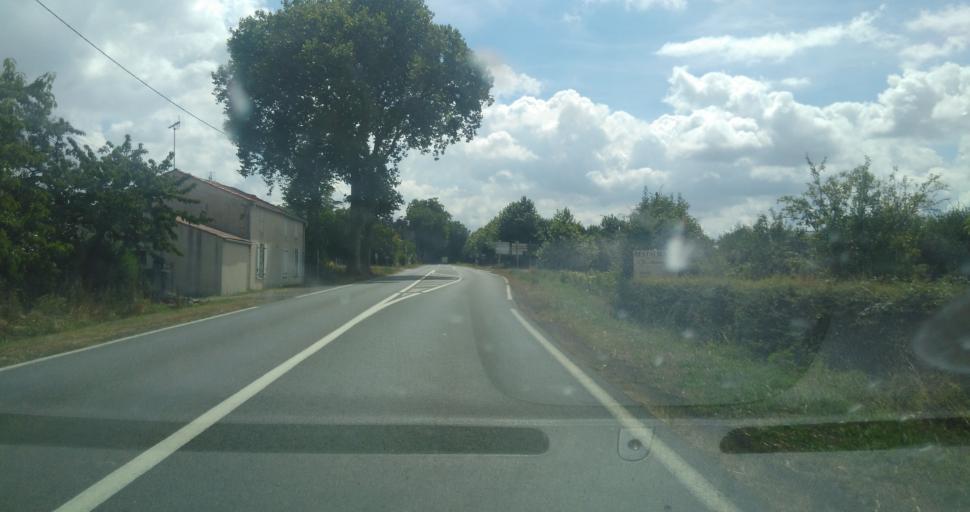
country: FR
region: Pays de la Loire
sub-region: Departement de la Vendee
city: Sainte-Hermine
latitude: 46.5647
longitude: -1.0784
